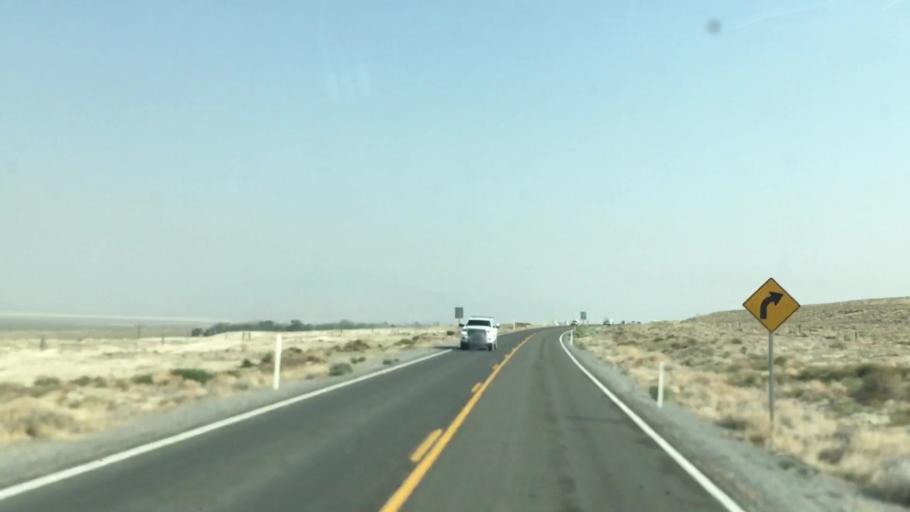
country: US
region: Nevada
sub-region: Pershing County
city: Lovelock
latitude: 40.5639
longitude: -119.3395
